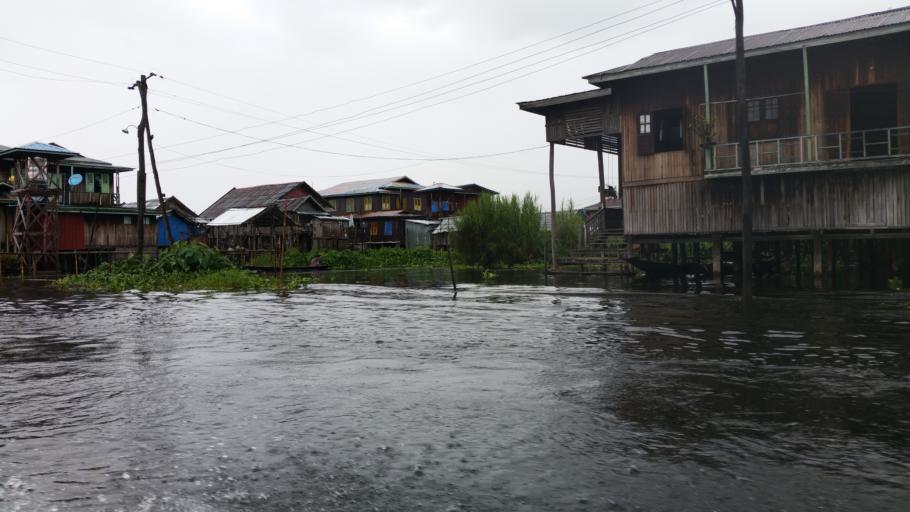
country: MM
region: Shan
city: Taunggyi
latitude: 20.5049
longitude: 96.9030
